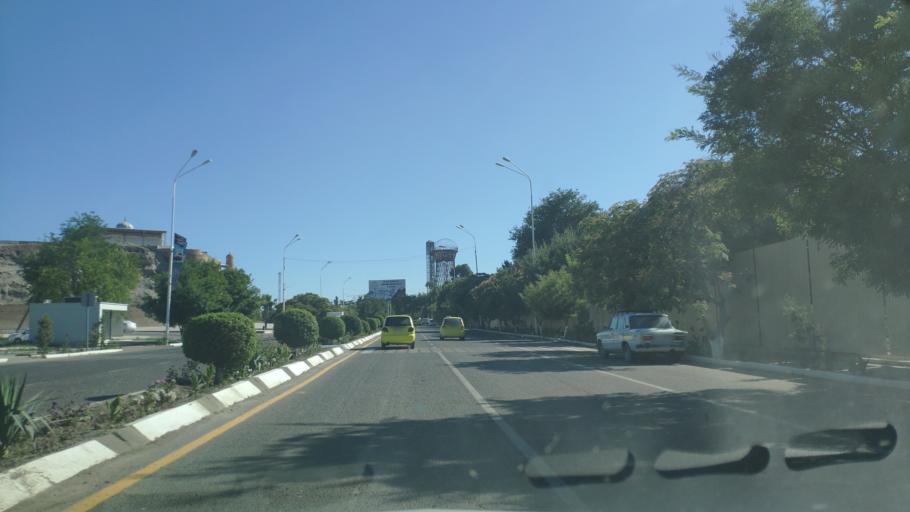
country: UZ
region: Bukhara
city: Bukhara
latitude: 39.7799
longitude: 64.4103
